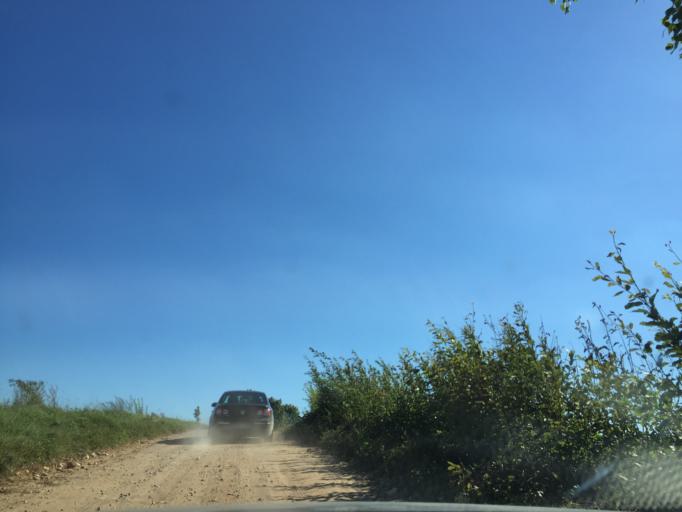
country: LT
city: Zarasai
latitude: 55.7932
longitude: 25.9534
